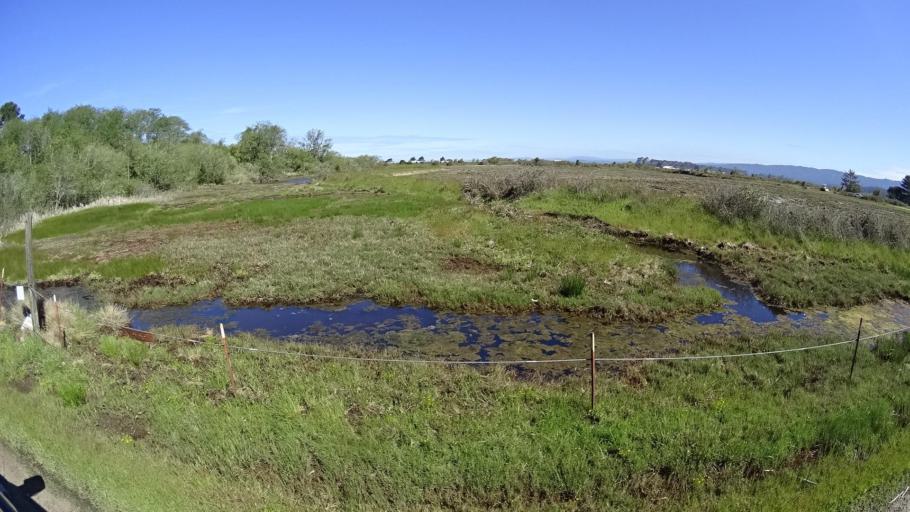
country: US
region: California
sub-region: Humboldt County
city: Myrtletown
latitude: 40.7950
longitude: -124.1230
